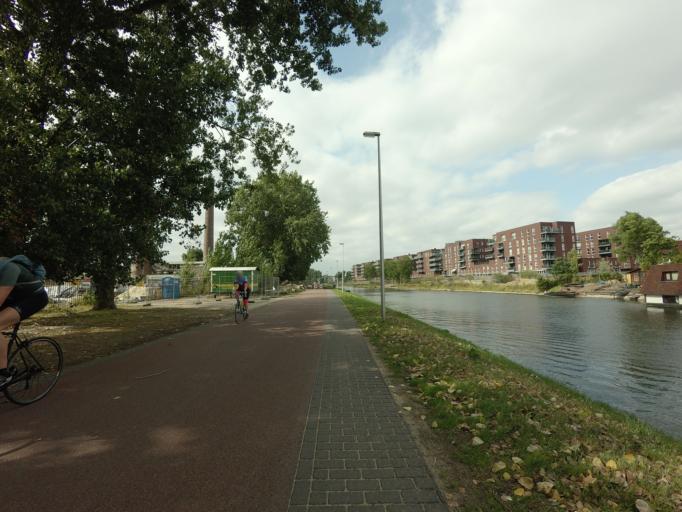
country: NL
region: Utrecht
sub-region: Gemeente Utrecht
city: Utrecht
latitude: 52.0782
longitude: 5.1086
